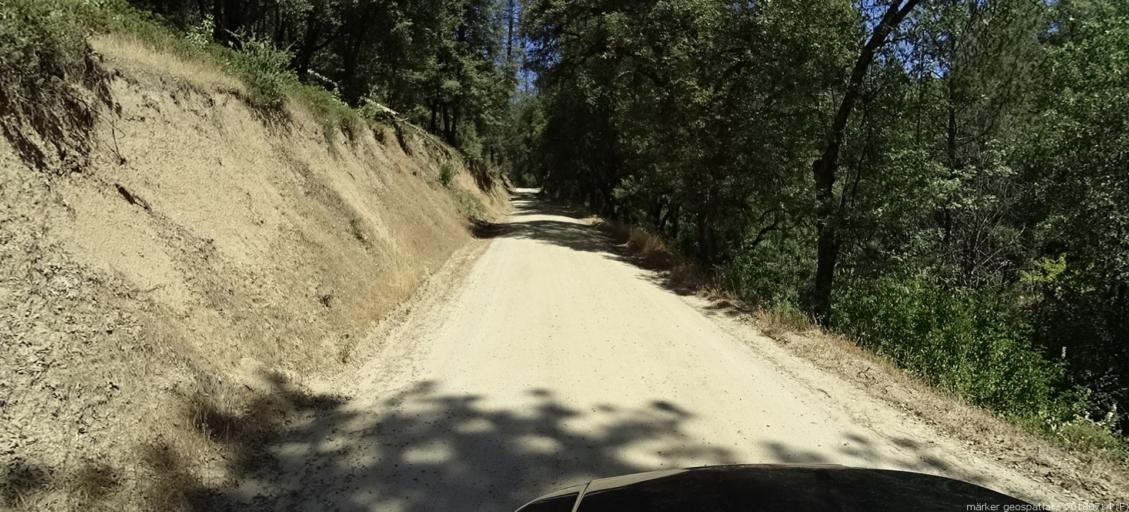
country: US
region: California
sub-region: Madera County
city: Ahwahnee
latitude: 37.3919
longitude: -119.6893
